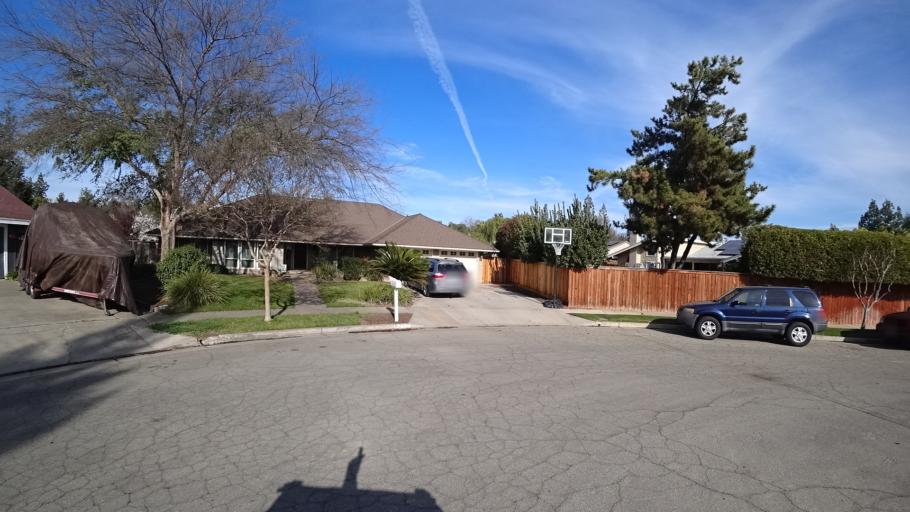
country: US
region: California
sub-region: Fresno County
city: Clovis
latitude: 36.8629
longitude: -119.7791
